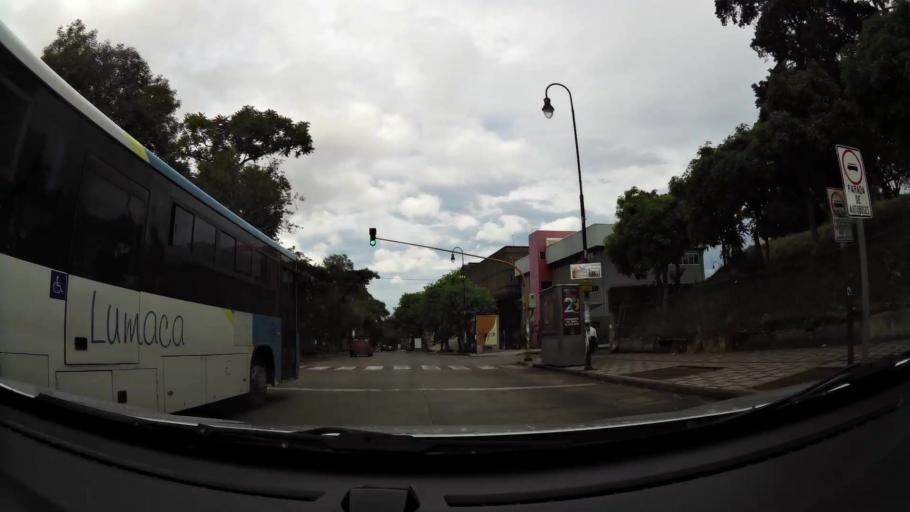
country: CR
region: San Jose
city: San Jose
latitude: 9.9351
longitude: -84.0705
